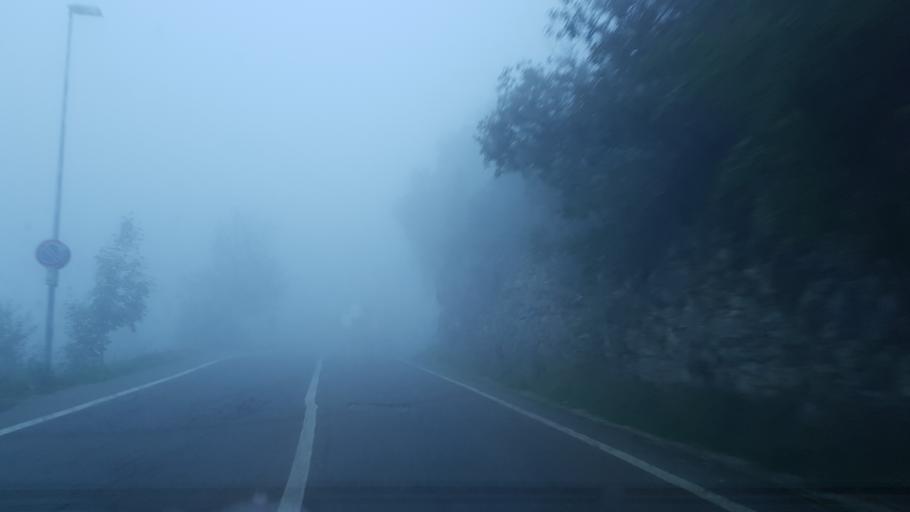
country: IT
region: Piedmont
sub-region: Provincia di Cuneo
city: Frabosa Soprana
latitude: 44.2543
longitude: 7.7794
